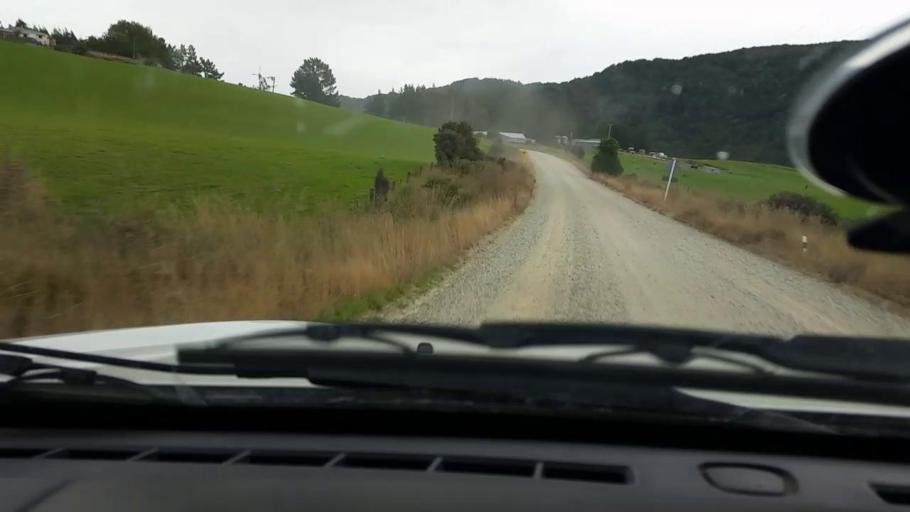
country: NZ
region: Otago
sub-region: Clutha District
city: Papatowai
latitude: -46.4616
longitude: 169.1217
